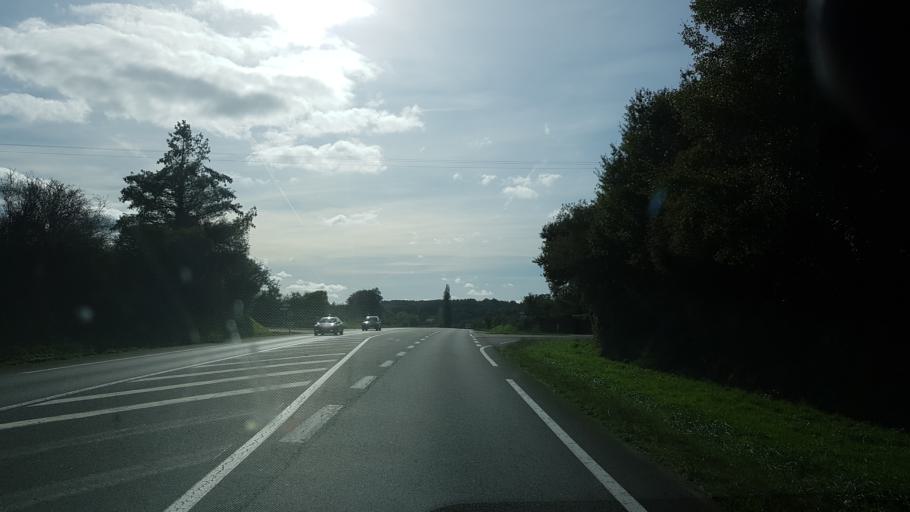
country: FR
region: Poitou-Charentes
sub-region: Departement de la Charente
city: Confolens
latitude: 46.0076
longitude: 0.6409
